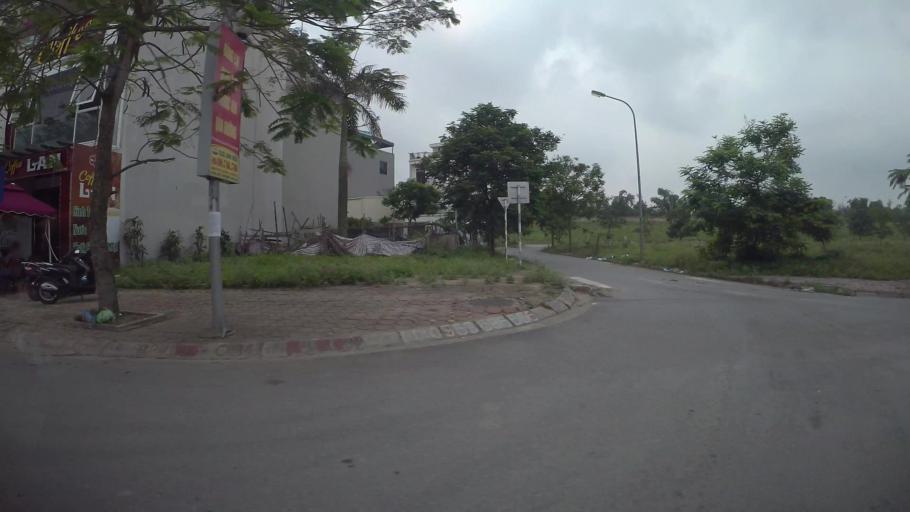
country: VN
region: Ha Noi
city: Trau Quy
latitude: 21.0564
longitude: 105.9177
